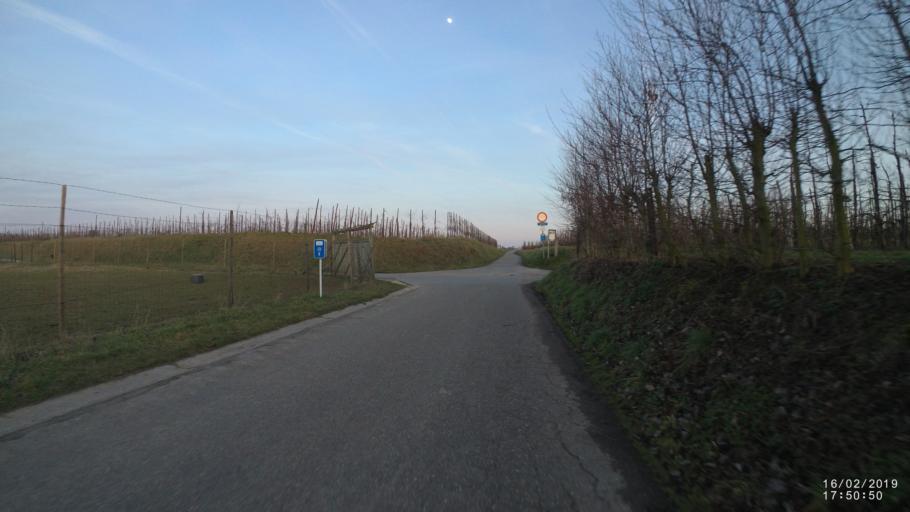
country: BE
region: Flanders
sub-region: Provincie Limburg
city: Sint-Truiden
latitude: 50.8167
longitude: 5.1480
